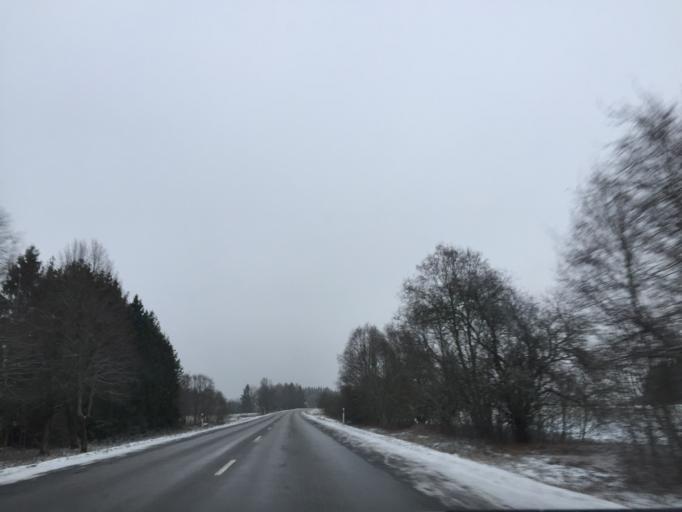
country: EE
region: Laeaene
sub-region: Lihula vald
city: Lihula
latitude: 58.5636
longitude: 23.9872
